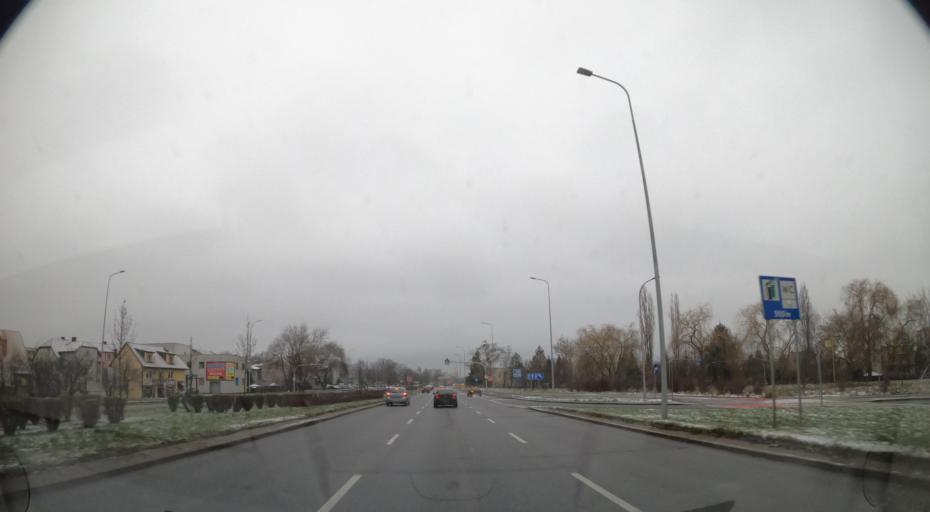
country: PL
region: Masovian Voivodeship
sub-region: Plock
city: Plock
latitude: 52.5442
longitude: 19.7154
